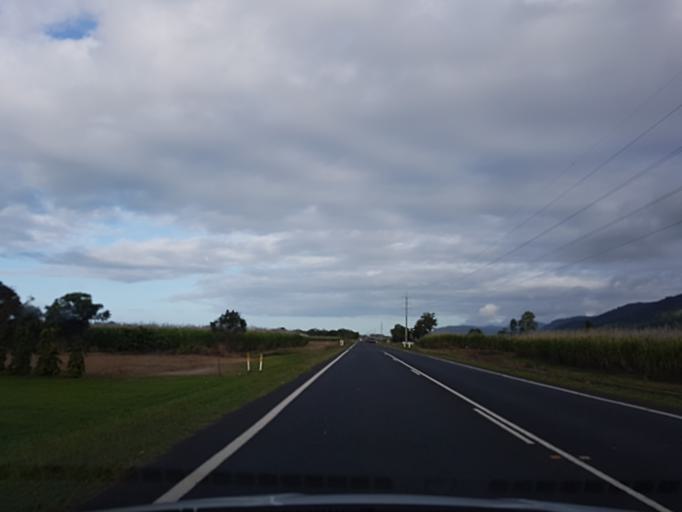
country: AU
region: Queensland
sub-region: Cairns
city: Port Douglas
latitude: -16.4941
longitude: 145.4241
